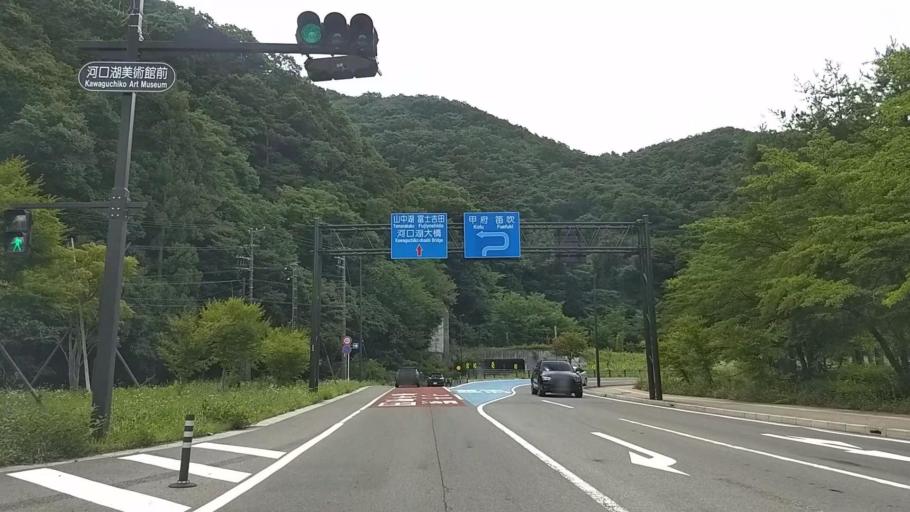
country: JP
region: Yamanashi
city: Fujikawaguchiko
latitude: 35.5187
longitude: 138.7719
